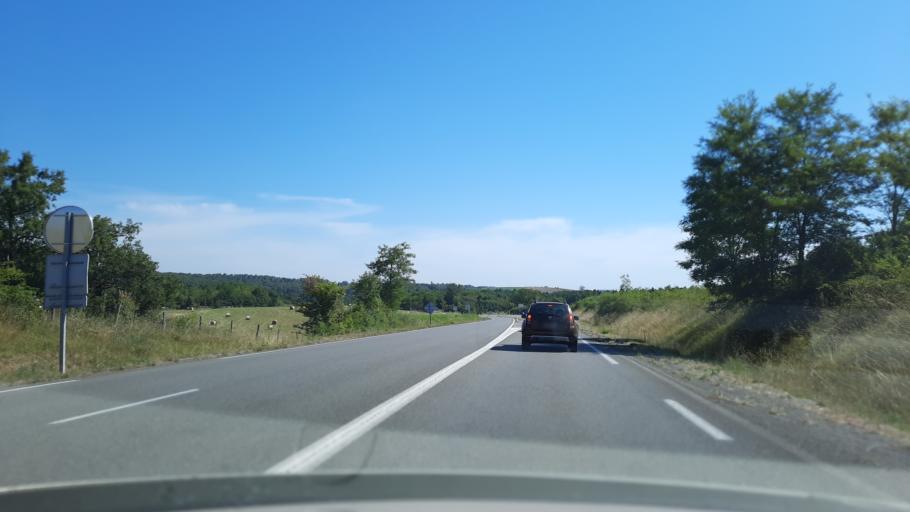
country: FR
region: Midi-Pyrenees
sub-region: Departement de l'Aveyron
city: Villefranche-de-Rouergue
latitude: 44.3346
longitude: 1.9353
